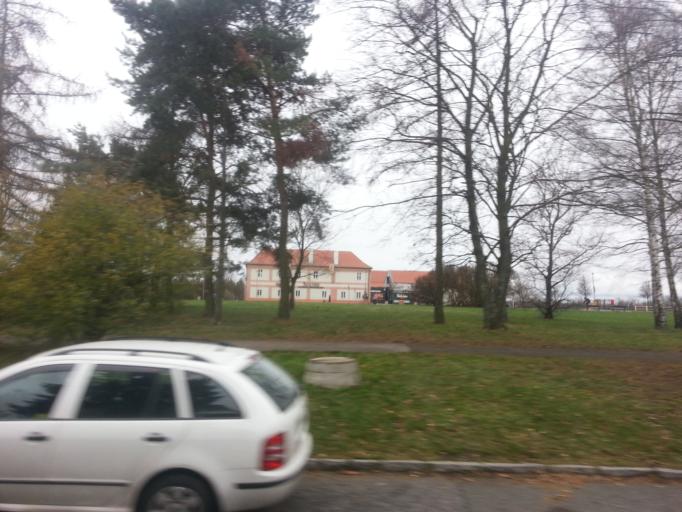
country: CZ
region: Praha
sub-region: Praha 1
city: Mala Strana
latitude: 50.0797
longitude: 14.3565
